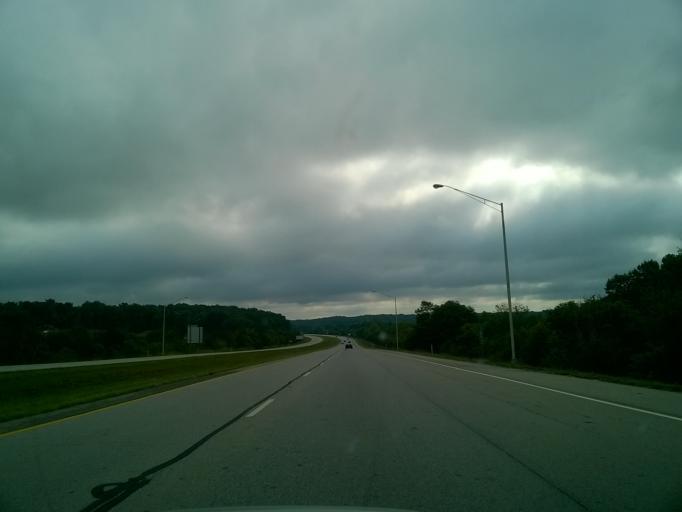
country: US
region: Indiana
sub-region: Harrison County
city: Corydon
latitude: 38.2396
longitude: -86.1225
